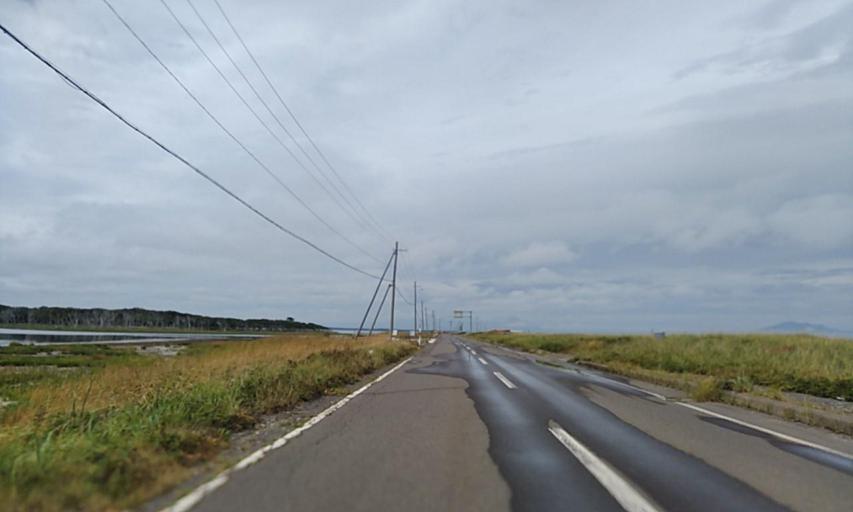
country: JP
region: Hokkaido
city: Shibetsu
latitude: 43.6087
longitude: 145.2762
